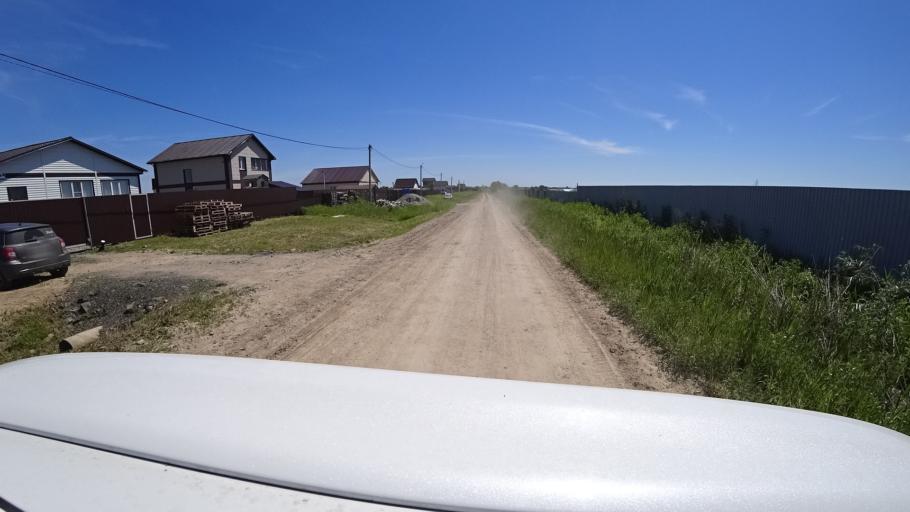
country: RU
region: Khabarovsk Krai
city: Topolevo
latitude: 48.5099
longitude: 135.2013
